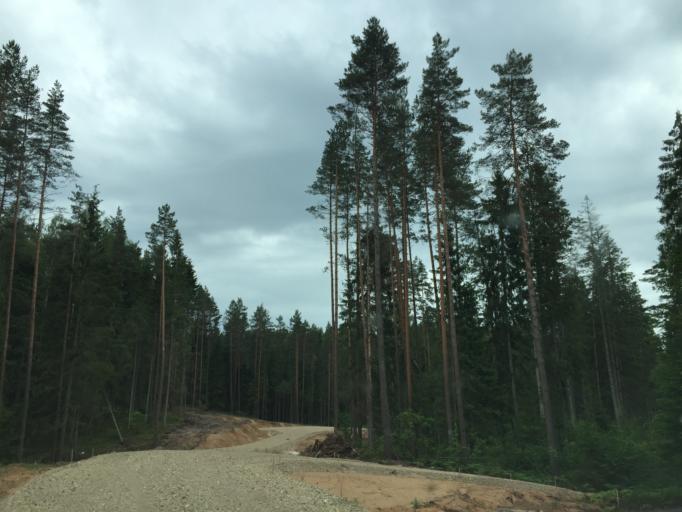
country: LV
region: Tukuma Rajons
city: Tukums
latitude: 57.0327
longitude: 23.0759
